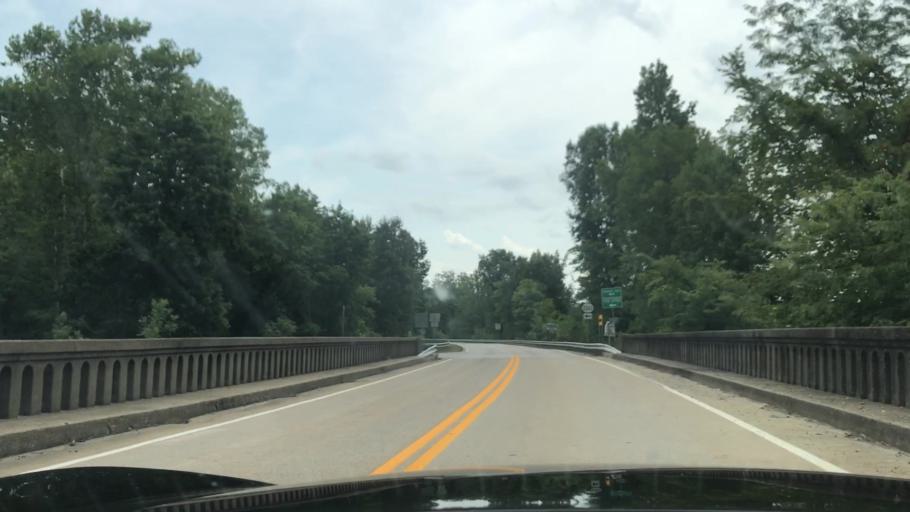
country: US
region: Kentucky
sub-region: Ohio County
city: Beaver Dam
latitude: 37.2104
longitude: -86.9003
